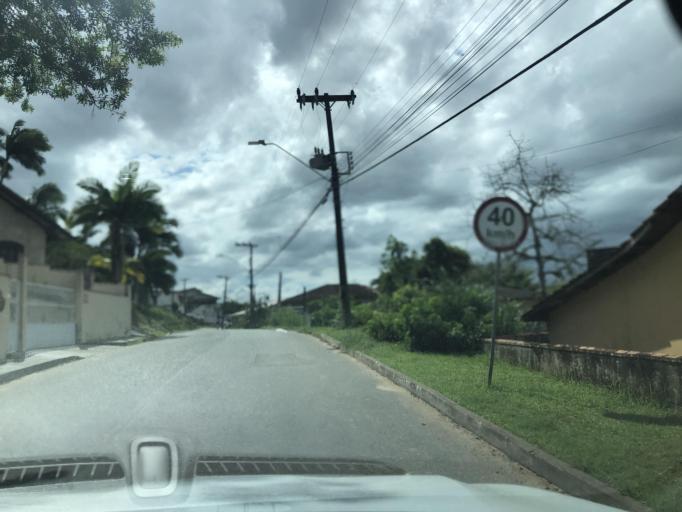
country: BR
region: Santa Catarina
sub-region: Sao Francisco Do Sul
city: Sao Francisco do Sul
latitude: -26.2307
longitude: -48.6097
